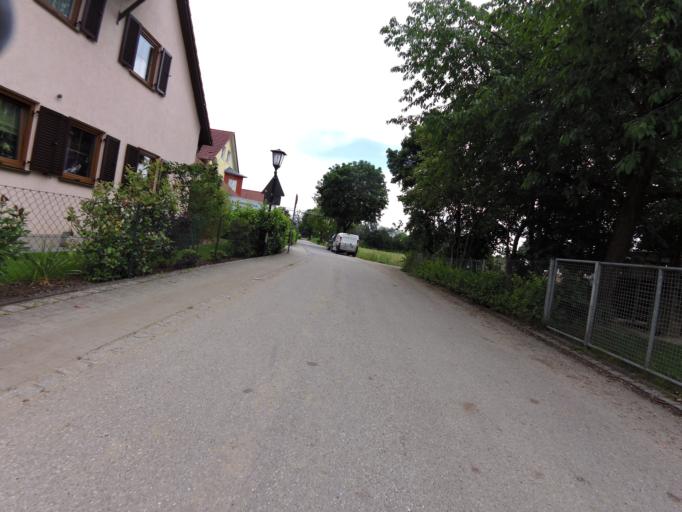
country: DE
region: Bavaria
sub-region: Upper Bavaria
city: Fahrenzhausen
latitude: 48.3510
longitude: 11.5601
